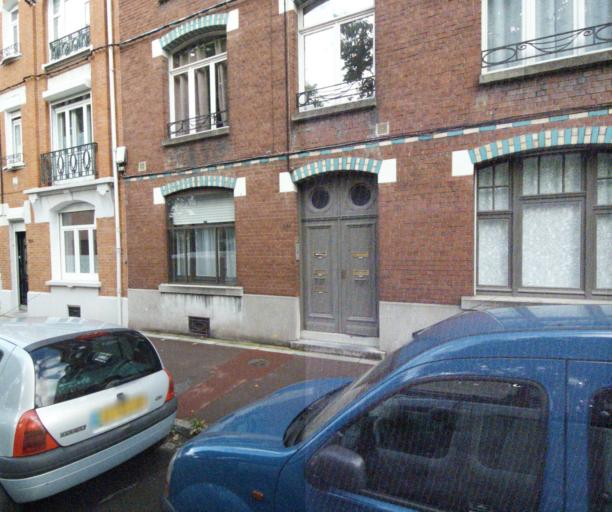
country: FR
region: Nord-Pas-de-Calais
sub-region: Departement du Nord
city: Loos
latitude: 50.6236
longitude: 3.0308
